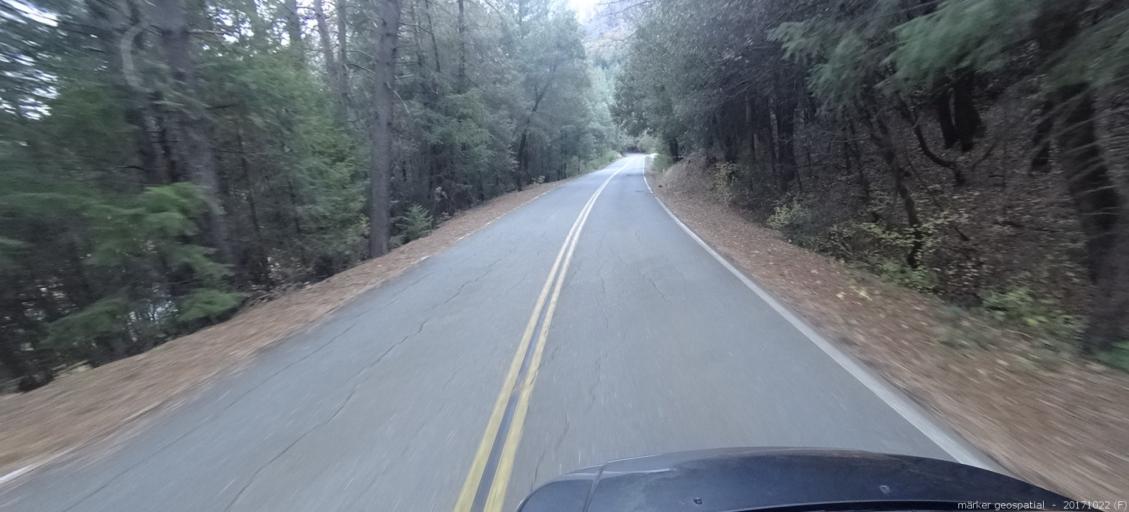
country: US
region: California
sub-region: Siskiyou County
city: Dunsmuir
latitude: 40.9350
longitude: -122.2488
